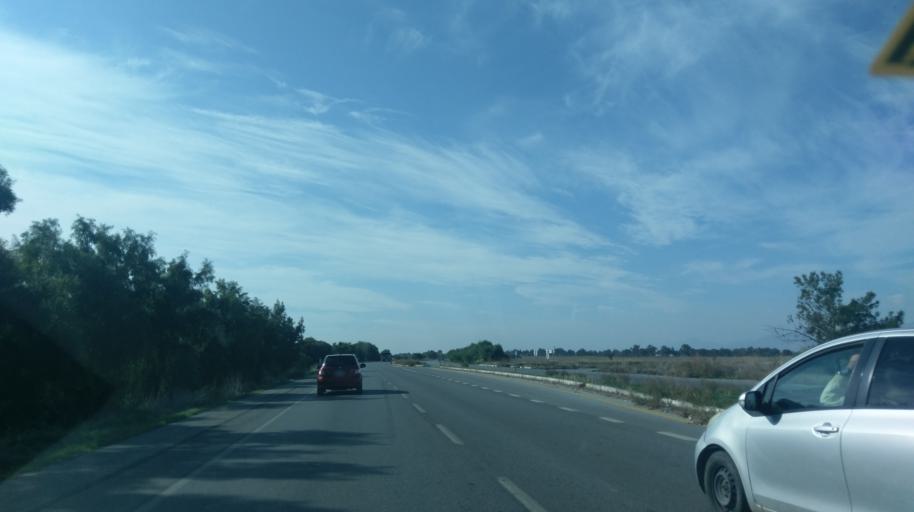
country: CY
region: Ammochostos
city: Lefkonoiko
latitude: 35.1784
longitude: 33.7422
